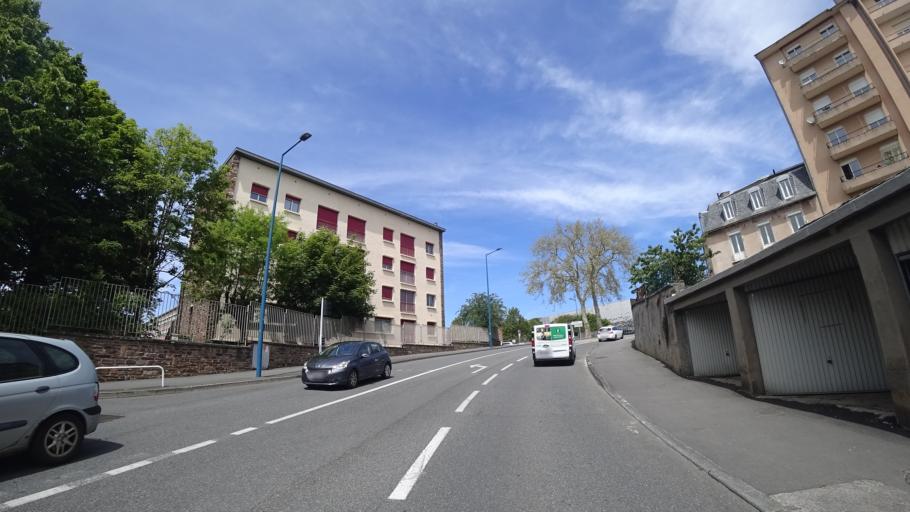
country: FR
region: Midi-Pyrenees
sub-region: Departement de l'Aveyron
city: Rodez
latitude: 44.3508
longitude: 2.5659
